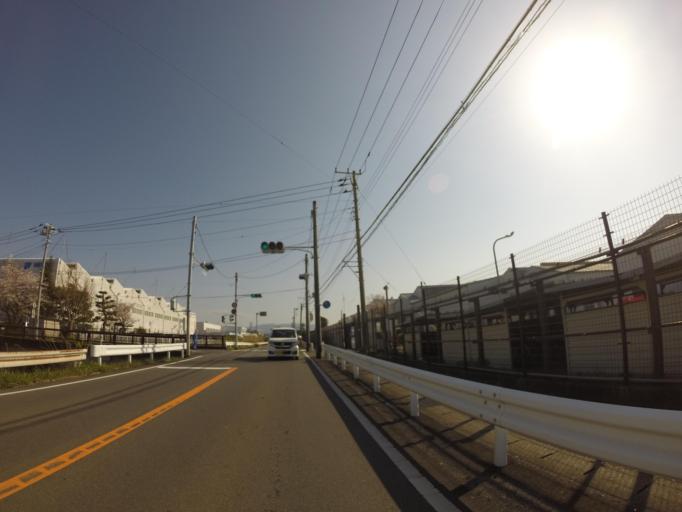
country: JP
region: Shizuoka
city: Numazu
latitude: 35.1103
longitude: 138.8486
